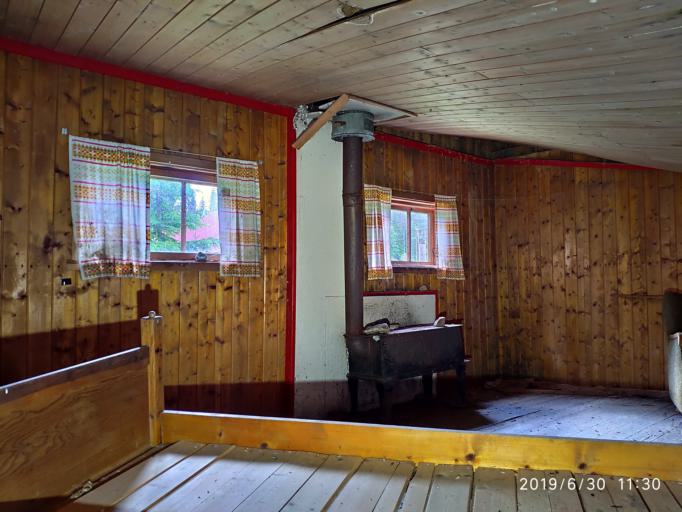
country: NO
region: Oppland
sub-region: Lunner
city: Grua
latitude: 60.2727
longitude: 10.7594
